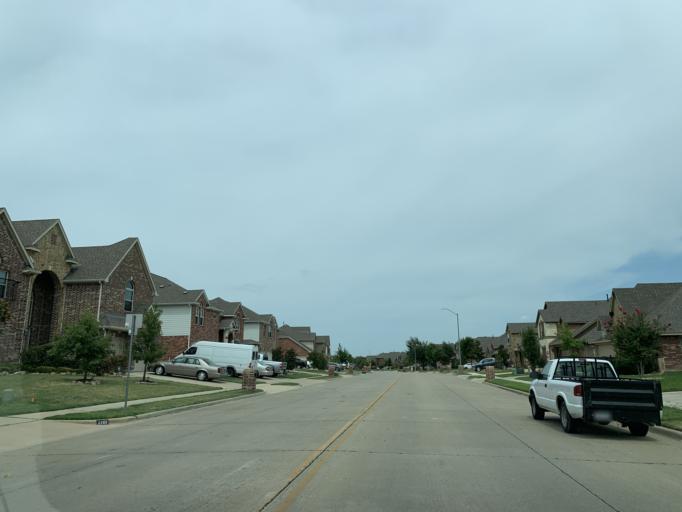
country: US
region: Texas
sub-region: Dallas County
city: Grand Prairie
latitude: 32.6515
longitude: -97.0389
